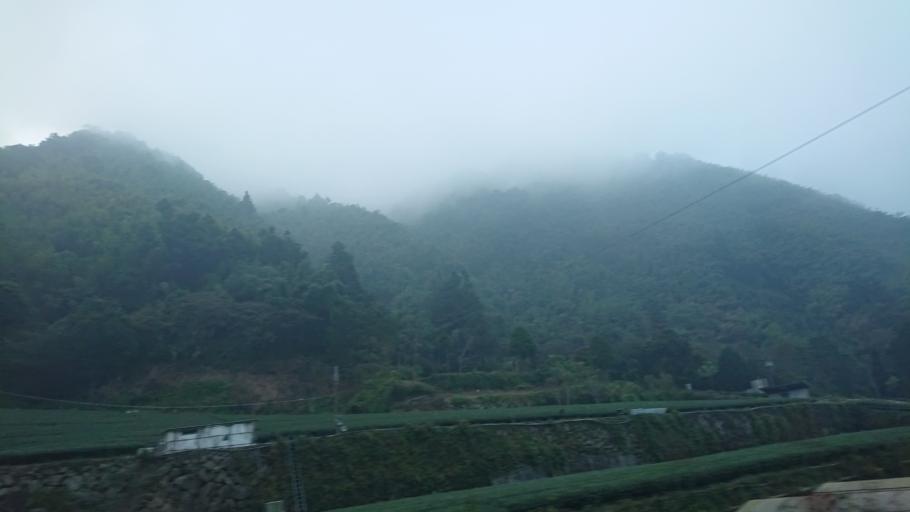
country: TW
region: Taiwan
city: Lugu
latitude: 23.5167
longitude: 120.6993
